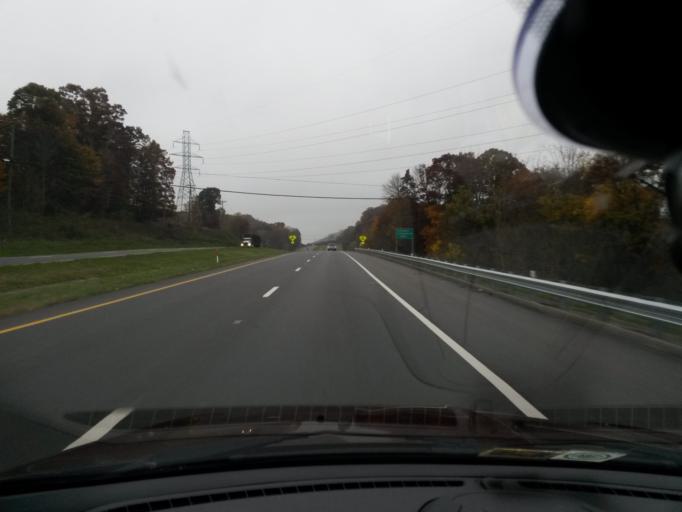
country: US
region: Virginia
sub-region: Botetourt County
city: Cloverdale
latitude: 37.3694
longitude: -79.8866
